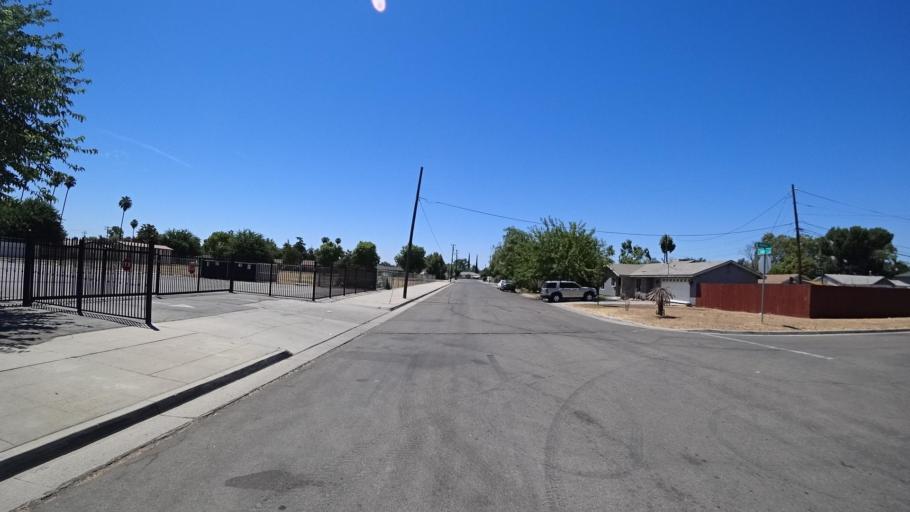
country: US
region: California
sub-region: Fresno County
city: Sunnyside
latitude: 36.7496
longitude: -119.7341
